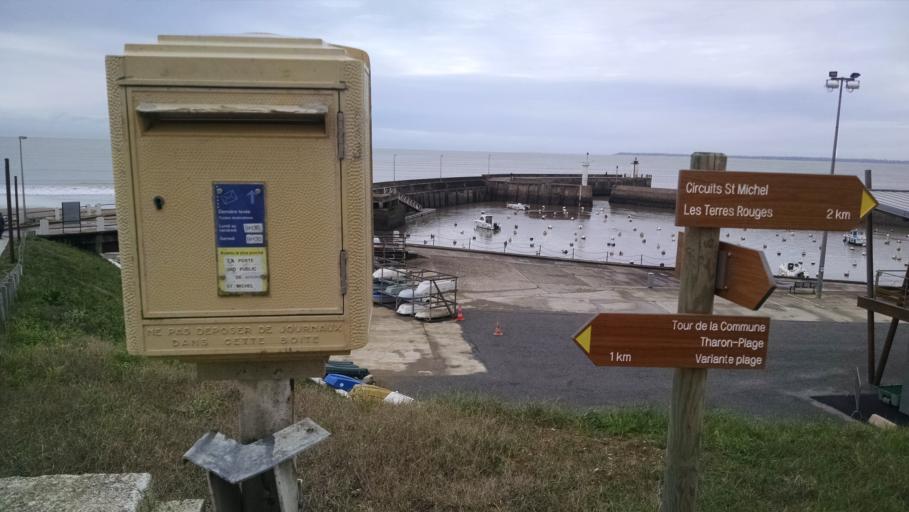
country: FR
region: Pays de la Loire
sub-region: Departement de la Loire-Atlantique
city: Saint-Michel-Chef-Chef
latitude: 47.1744
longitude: -2.1643
